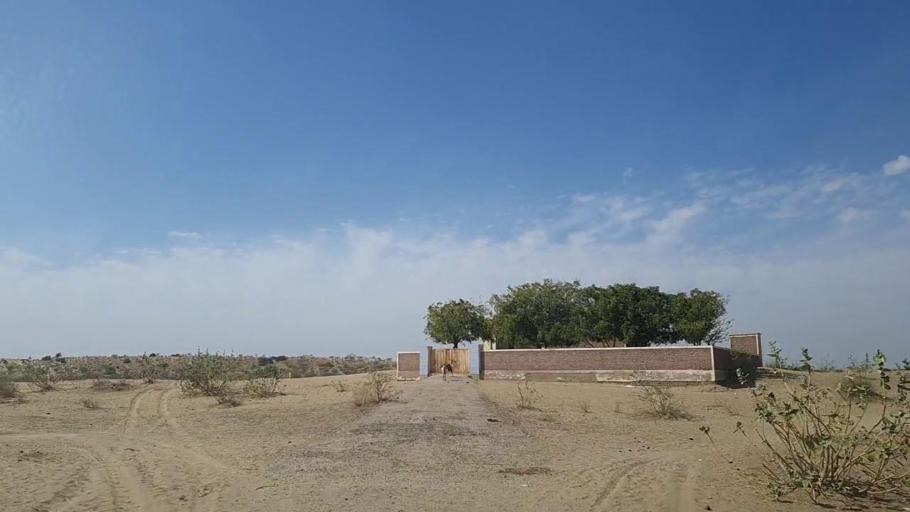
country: PK
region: Sindh
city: Nabisar
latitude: 24.8823
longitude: 69.6139
